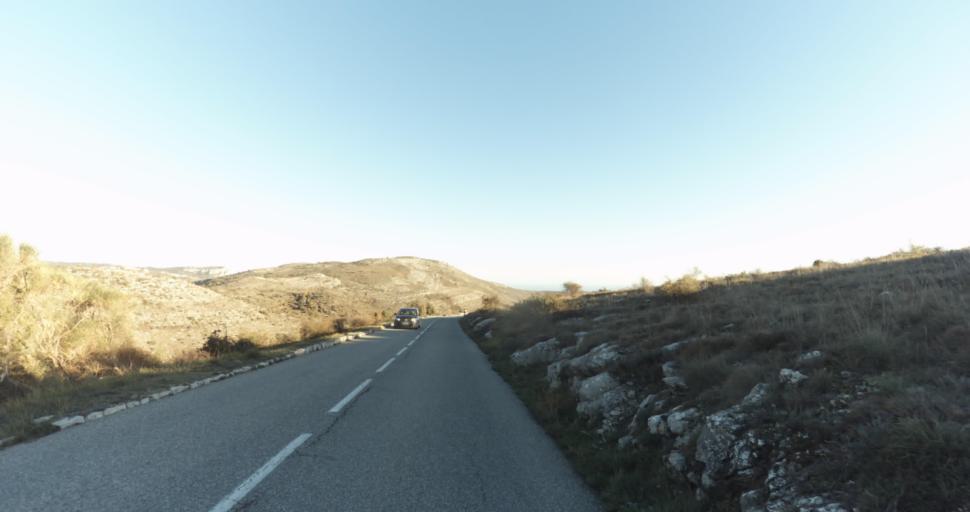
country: FR
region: Provence-Alpes-Cote d'Azur
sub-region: Departement des Alpes-Maritimes
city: Vence
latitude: 43.7544
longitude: 7.0898
